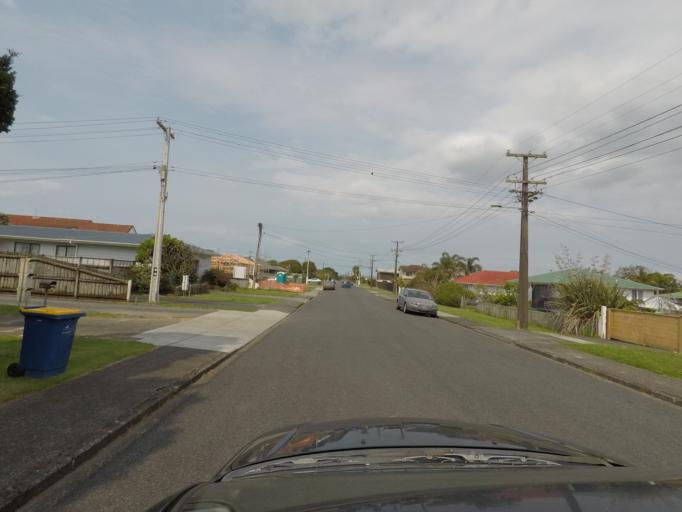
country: NZ
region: Auckland
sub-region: Auckland
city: Rosebank
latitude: -36.8289
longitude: 174.6450
